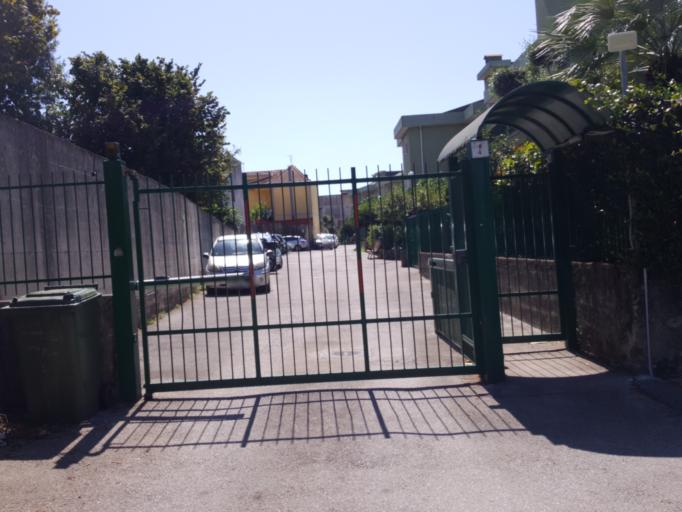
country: IT
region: Campania
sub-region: Provincia di Salerno
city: Baronissi
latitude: 40.7480
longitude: 14.7838
